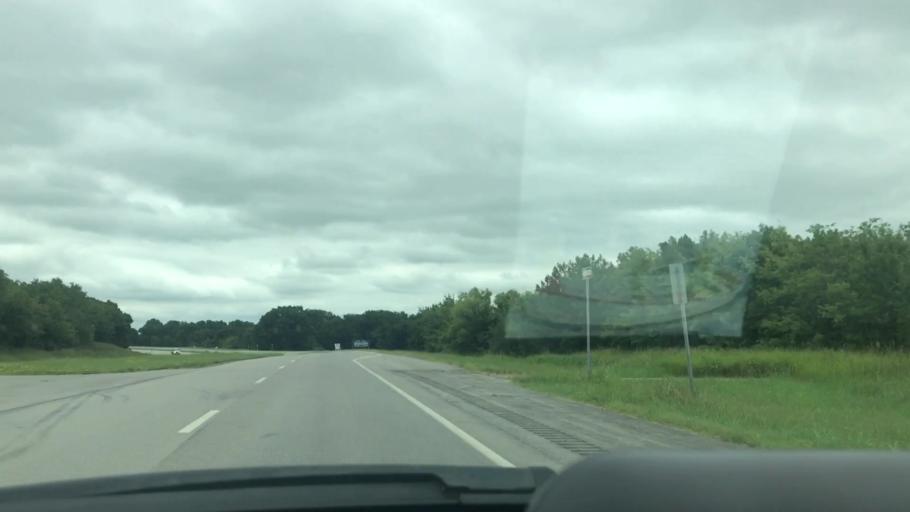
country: US
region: Oklahoma
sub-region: Mayes County
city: Pryor
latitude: 36.3625
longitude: -95.2942
